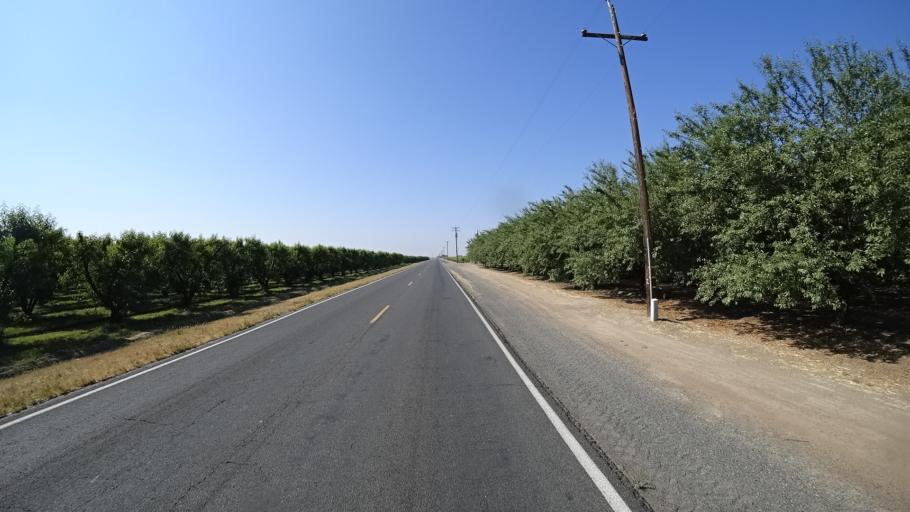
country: US
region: California
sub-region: Kings County
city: Lucerne
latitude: 36.3917
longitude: -119.5650
